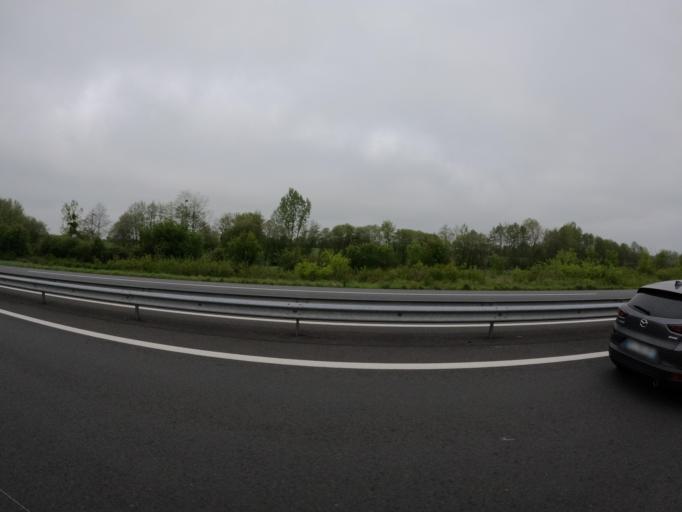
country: FR
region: Pays de la Loire
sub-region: Departement de la Vendee
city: Vendrennes
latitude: 46.8703
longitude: -1.1234
